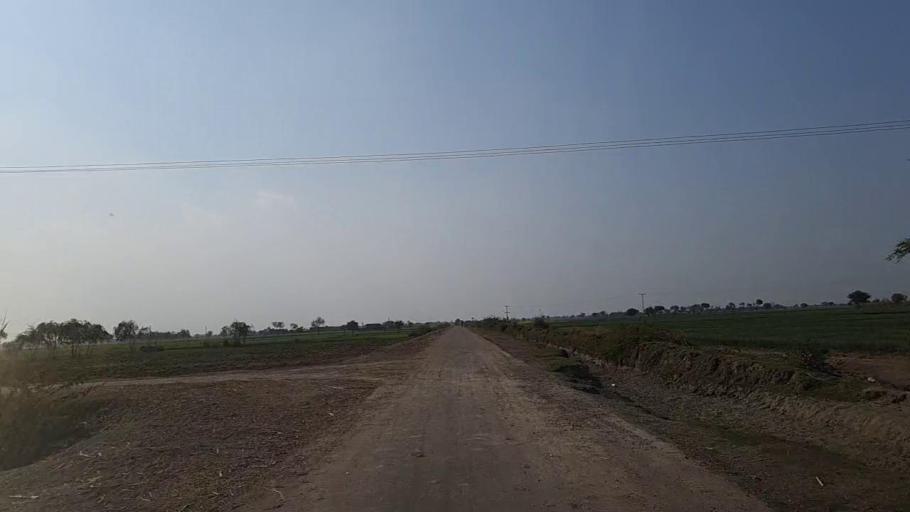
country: PK
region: Sindh
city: Jam Sahib
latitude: 26.3002
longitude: 68.5759
